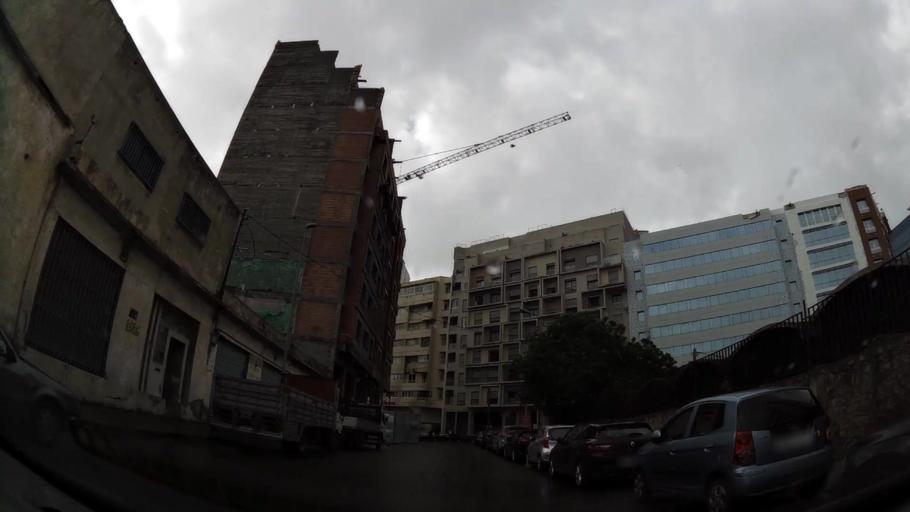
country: MA
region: Grand Casablanca
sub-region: Casablanca
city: Casablanca
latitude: 33.5943
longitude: -7.5989
